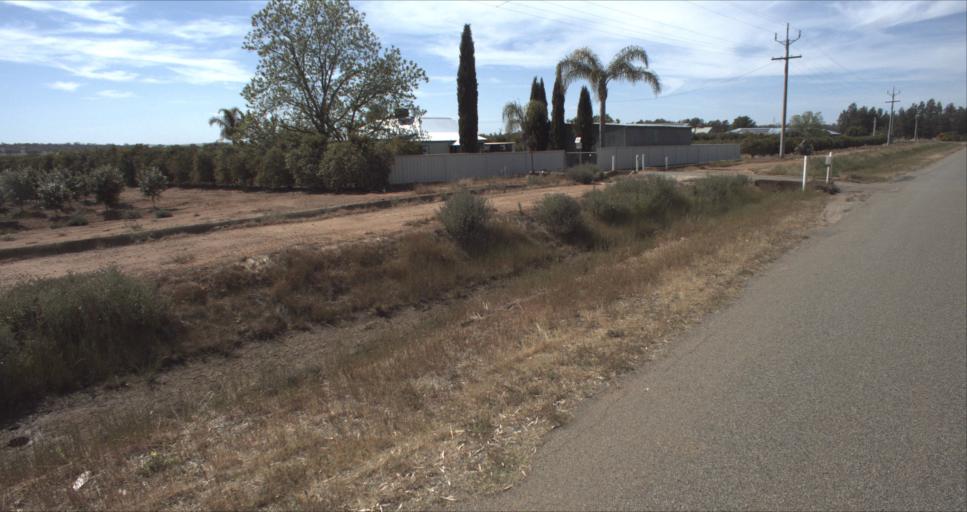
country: AU
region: New South Wales
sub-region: Leeton
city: Leeton
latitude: -34.5885
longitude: 146.4618
